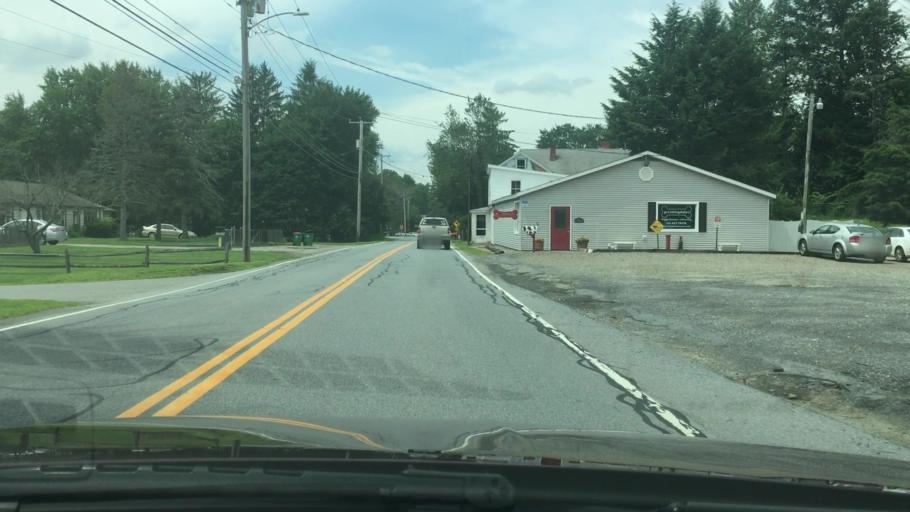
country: US
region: New York
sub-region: Dutchess County
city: Hillside Lake
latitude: 41.6508
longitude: -73.7616
